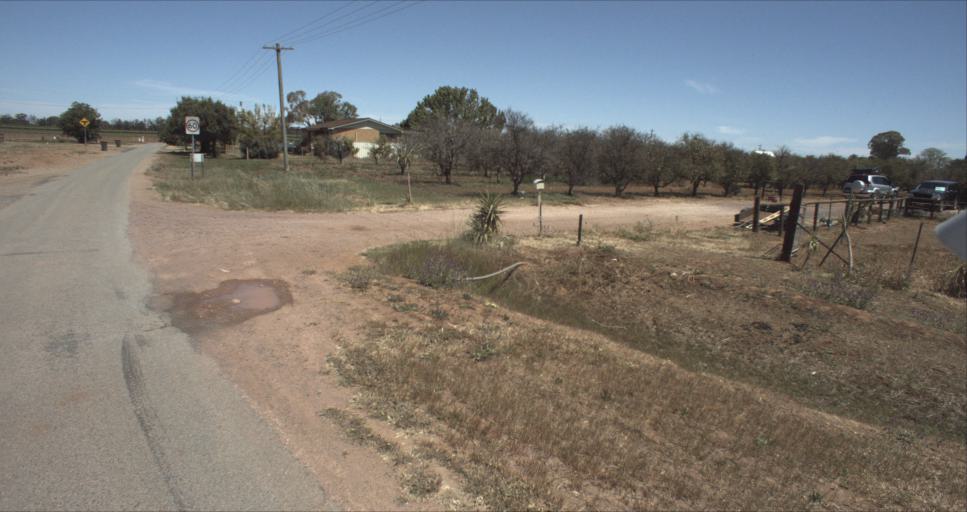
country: AU
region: New South Wales
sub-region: Leeton
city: Leeton
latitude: -34.5298
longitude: 146.3333
